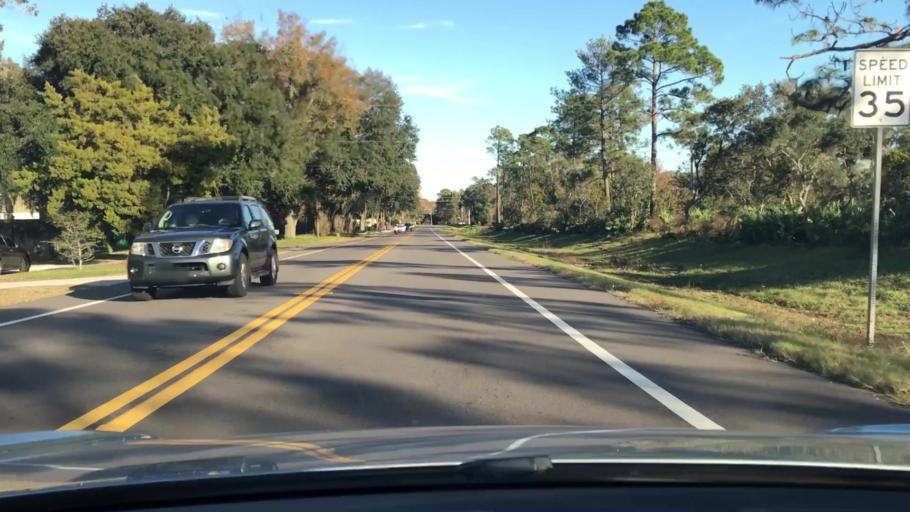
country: US
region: Florida
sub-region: Saint Johns County
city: Villano Beach
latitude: 29.9312
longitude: -81.3488
